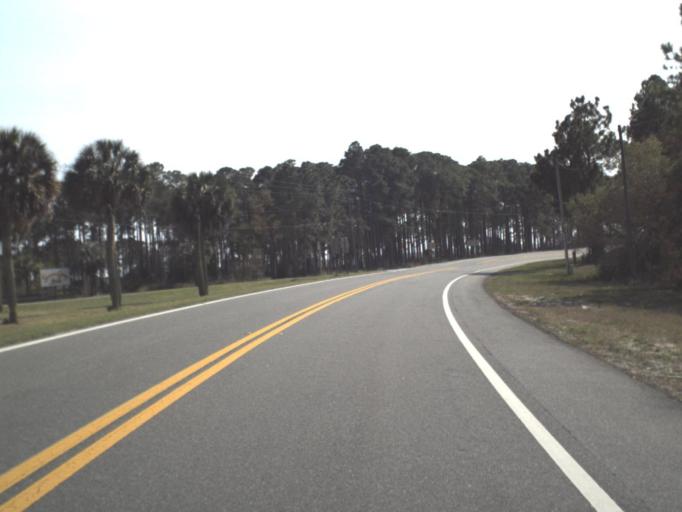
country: US
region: Florida
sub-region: Franklin County
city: Carrabelle
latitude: 29.9194
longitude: -84.5203
